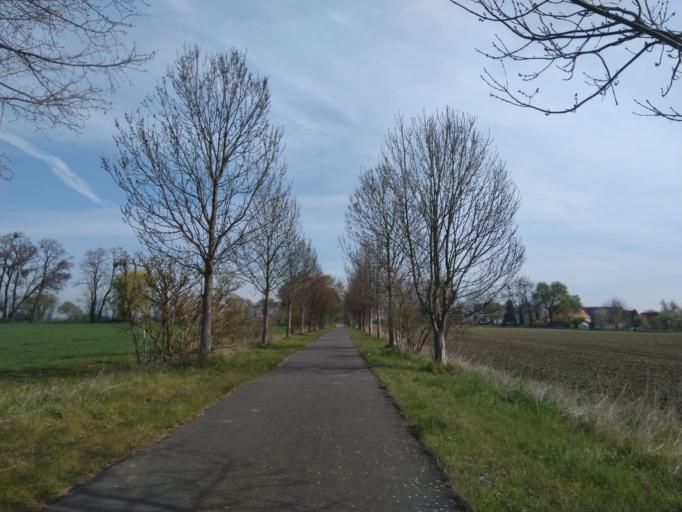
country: DE
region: Brandenburg
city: Wriezen
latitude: 52.7394
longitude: 14.1583
